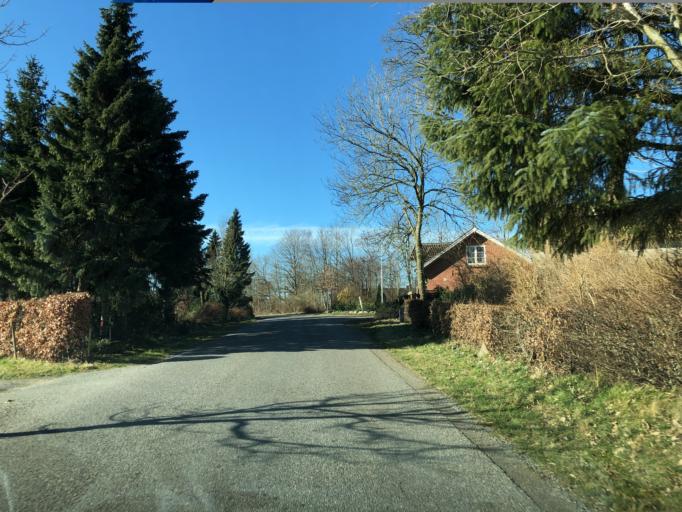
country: DK
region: Central Jutland
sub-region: Ikast-Brande Kommune
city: Bording Kirkeby
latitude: 56.1558
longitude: 9.2361
